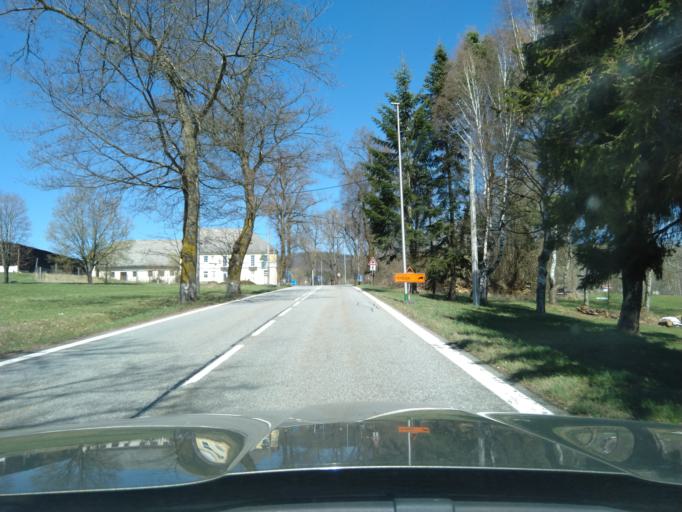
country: CZ
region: Jihocesky
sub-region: Okres Prachatice
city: Borova Lada
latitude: 48.9593
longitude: 13.7575
